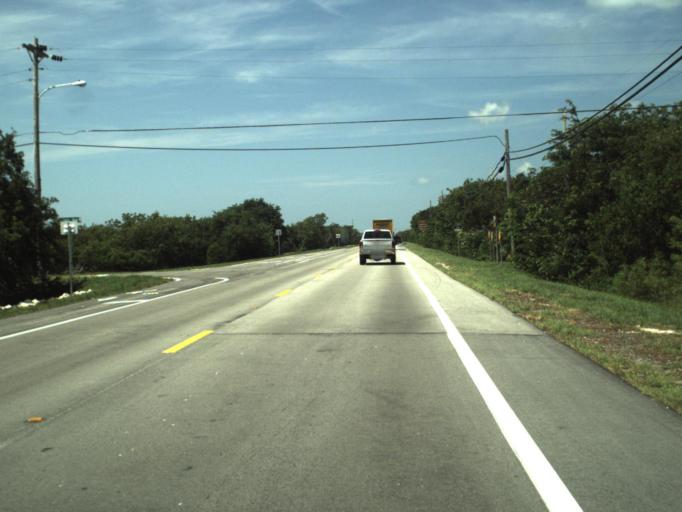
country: US
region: Florida
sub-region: Monroe County
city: Marathon
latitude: 24.7484
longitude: -80.9783
